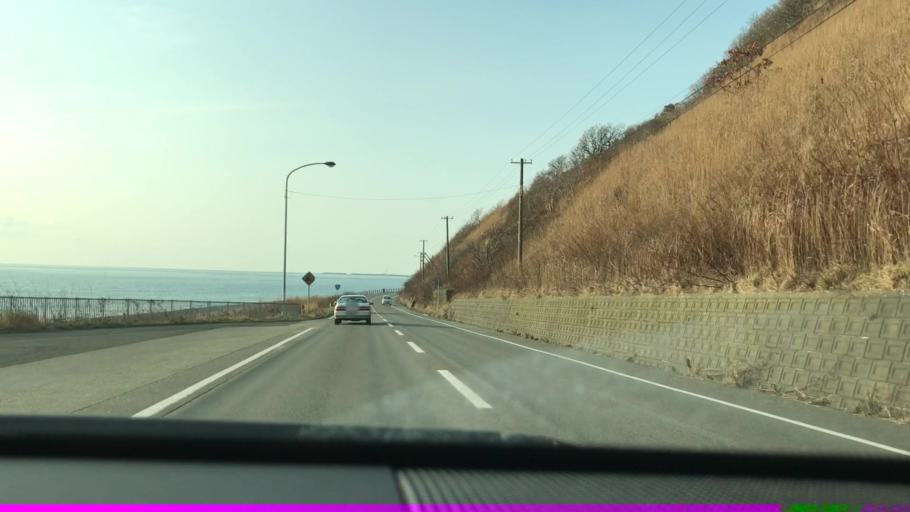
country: JP
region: Hokkaido
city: Shizunai-furukawacho
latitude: 42.2326
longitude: 142.6056
